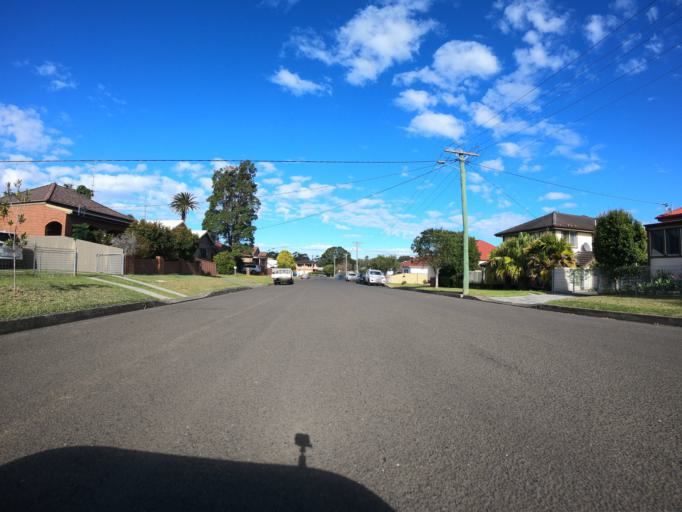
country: AU
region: New South Wales
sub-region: Wollongong
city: Corrimal
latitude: -34.3710
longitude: 150.9026
